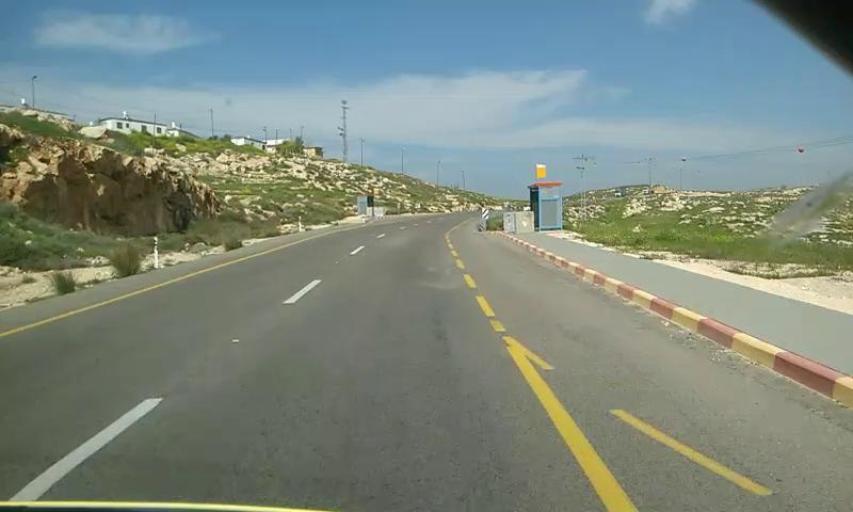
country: PS
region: West Bank
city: Az Zahiriyah
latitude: 31.3922
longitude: 35.0162
